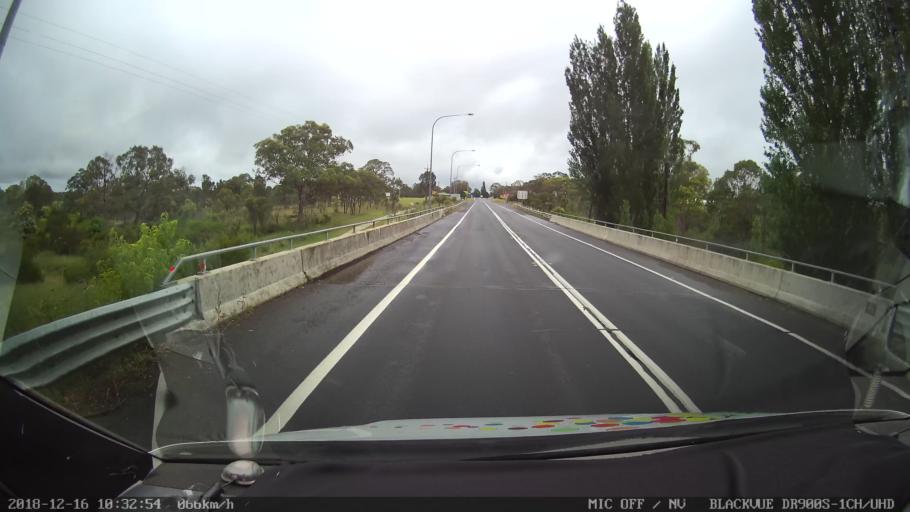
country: AU
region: New South Wales
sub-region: Tenterfield Municipality
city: Carrolls Creek
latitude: -29.0682
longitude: 152.0141
